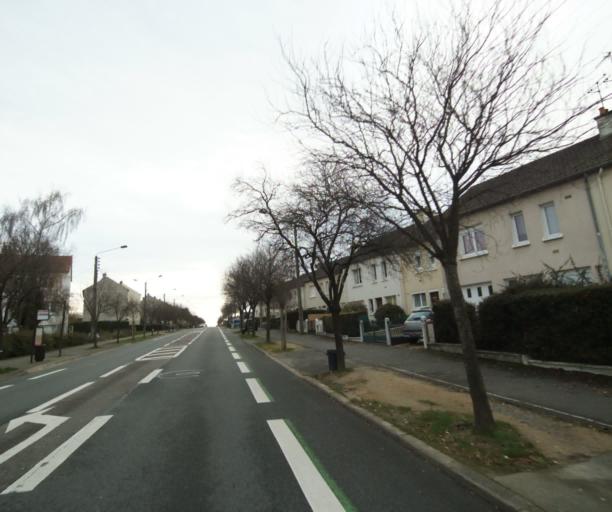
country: FR
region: Pays de la Loire
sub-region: Departement de la Sarthe
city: Coulaines
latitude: 48.0133
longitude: 0.2225
